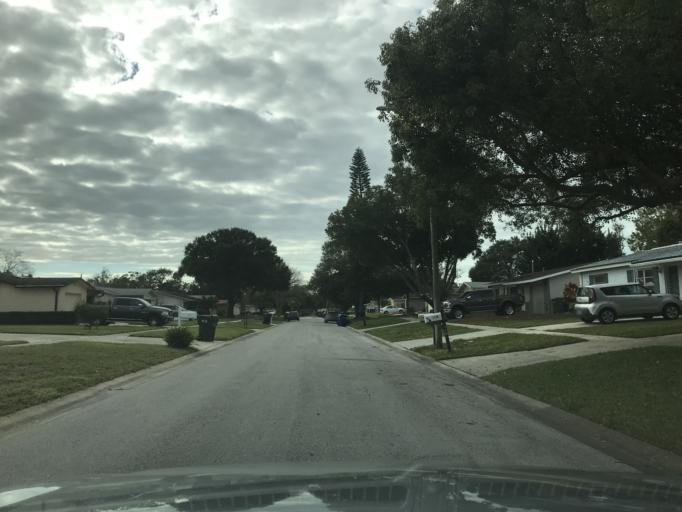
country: US
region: Florida
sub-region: Pinellas County
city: Largo
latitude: 27.9269
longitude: -82.7787
